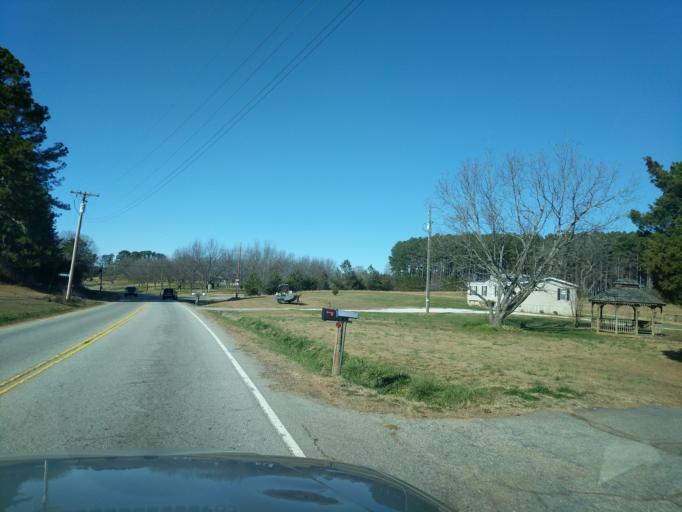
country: US
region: South Carolina
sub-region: Oconee County
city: Westminster
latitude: 34.6773
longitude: -83.1144
